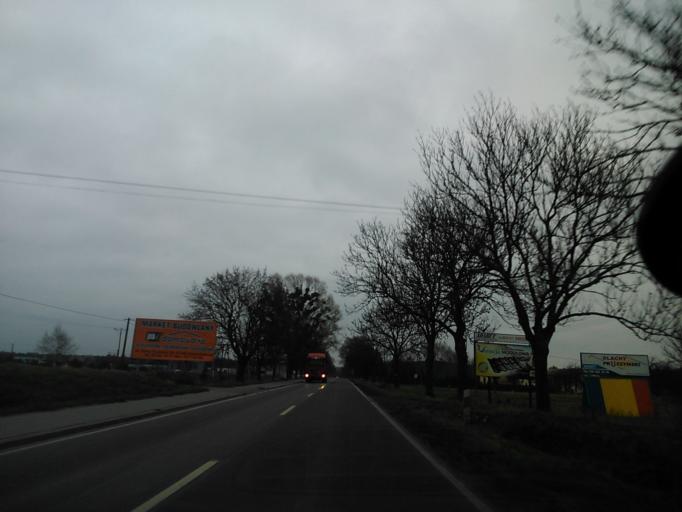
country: PL
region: Kujawsko-Pomorskie
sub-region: Powiat golubsko-dobrzynski
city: Golub-Dobrzyn
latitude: 53.1090
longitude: 19.0813
